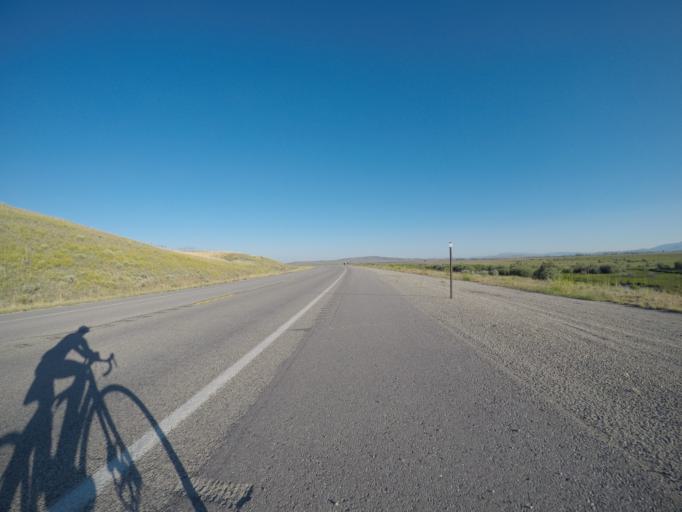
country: US
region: Wyoming
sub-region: Sublette County
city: Pinedale
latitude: 42.8742
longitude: -109.9359
